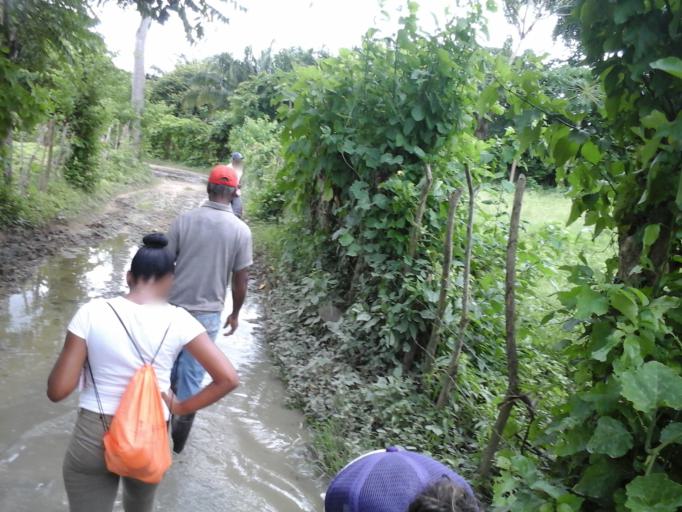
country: CO
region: Bolivar
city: San Pablo
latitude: 10.1563
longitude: -75.2741
